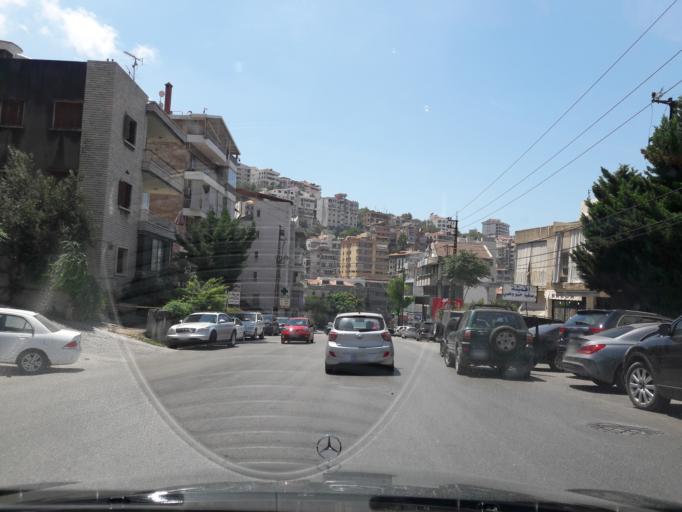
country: LB
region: Mont-Liban
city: Djounie
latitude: 33.9263
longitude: 35.6348
